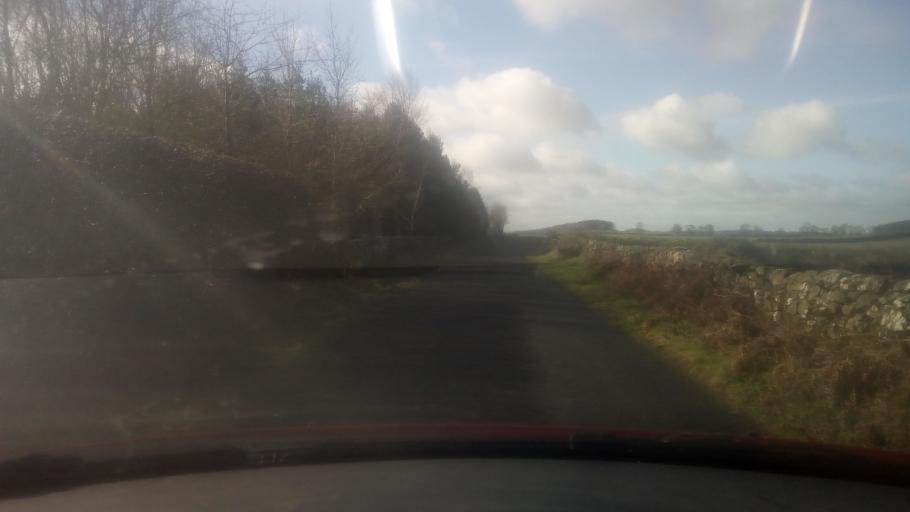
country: GB
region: Scotland
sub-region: The Scottish Borders
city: Jedburgh
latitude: 55.5325
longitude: -2.5663
